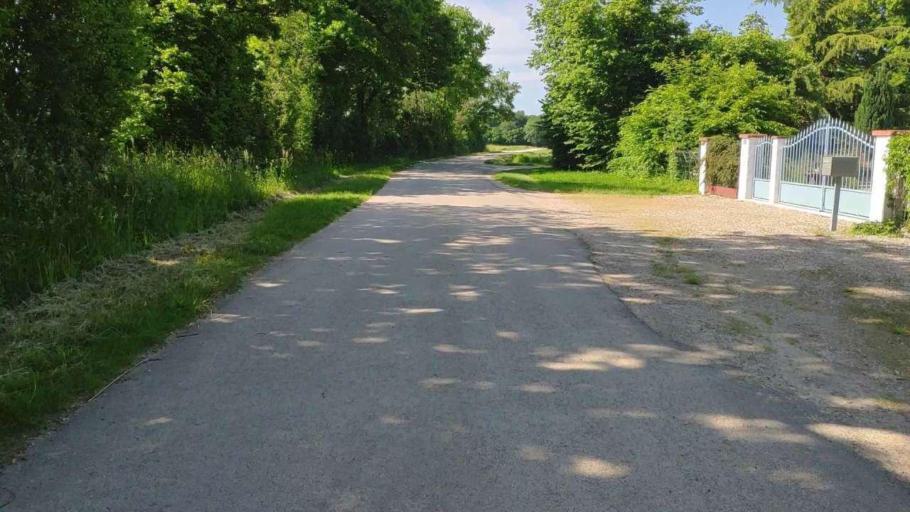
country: FR
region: Franche-Comte
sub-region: Departement du Jura
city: Bletterans
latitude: 46.7071
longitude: 5.4557
